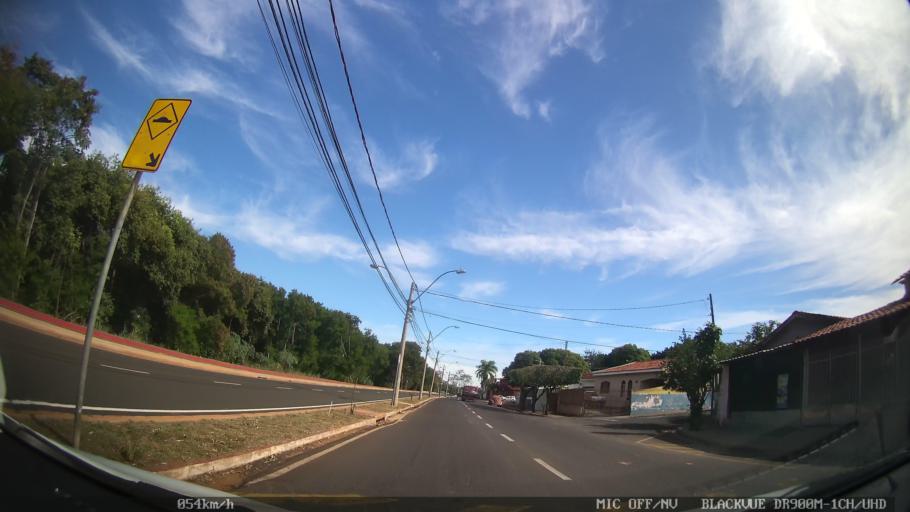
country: BR
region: Sao Paulo
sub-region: Sao Jose Do Rio Preto
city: Sao Jose do Rio Preto
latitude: -20.8395
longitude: -49.3488
